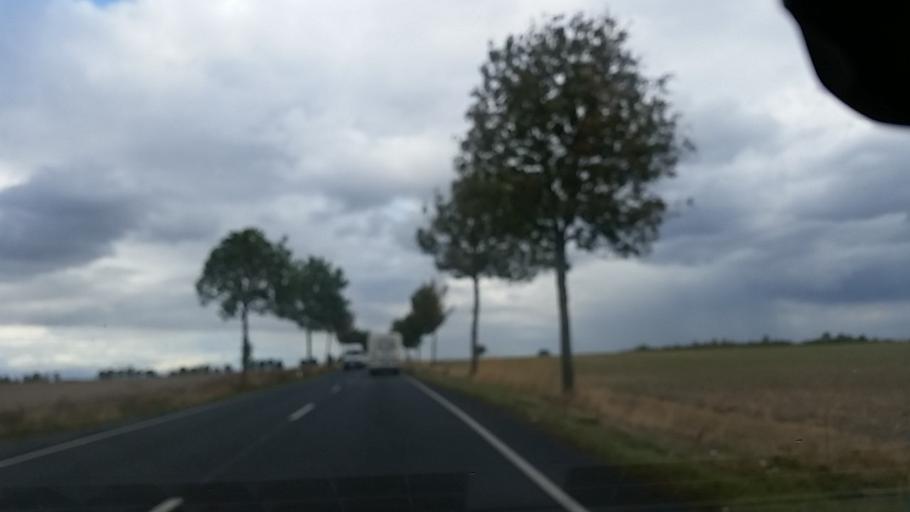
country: DE
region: Lower Saxony
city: Danndorf
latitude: 52.3994
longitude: 10.8498
